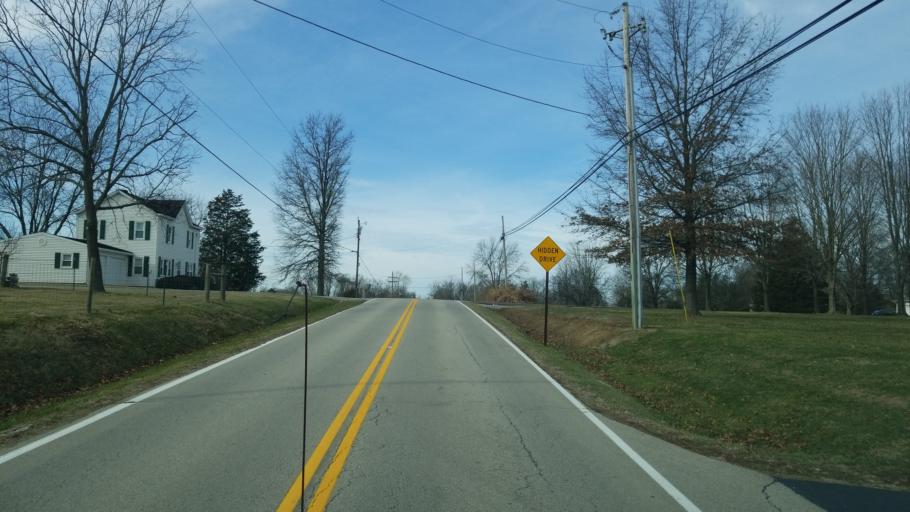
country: US
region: Ohio
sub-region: Warren County
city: Lebanon
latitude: 39.4289
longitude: -84.1399
